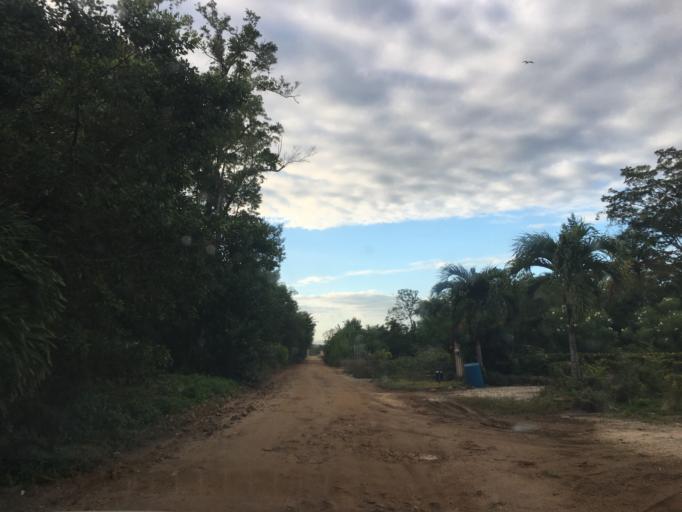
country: BZ
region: Stann Creek
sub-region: Dangriga
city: Dangriga
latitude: 16.8126
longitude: -88.2578
